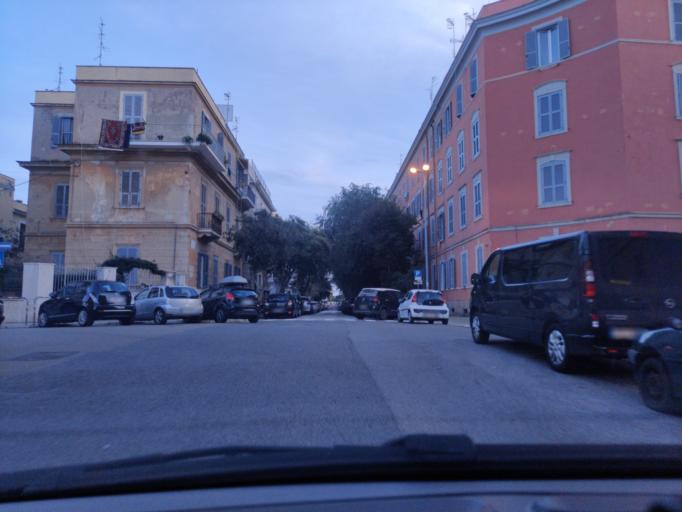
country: IT
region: Latium
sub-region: Citta metropolitana di Roma Capitale
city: Civitavecchia
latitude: 42.0946
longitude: 11.7933
